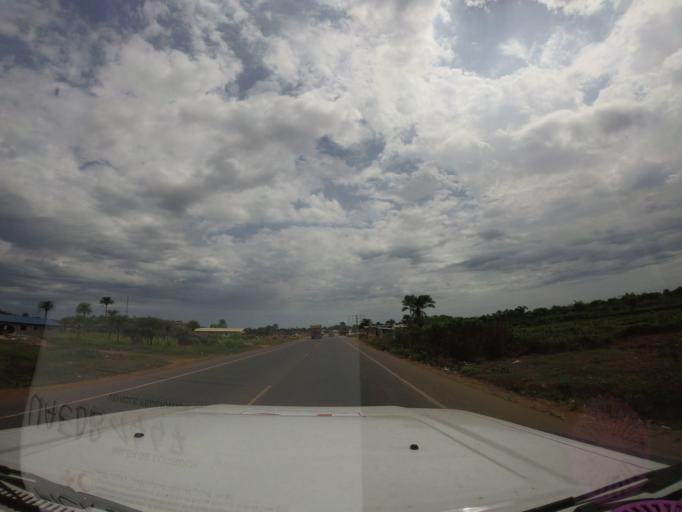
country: LR
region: Montserrado
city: Bensonville City
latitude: 6.3291
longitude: -10.6597
